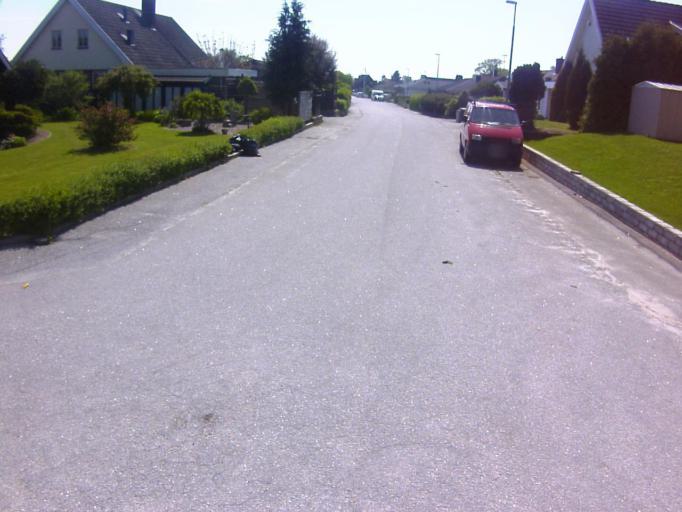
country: SE
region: Blekinge
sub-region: Solvesborgs Kommun
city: Soelvesborg
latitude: 56.0166
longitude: 14.6976
